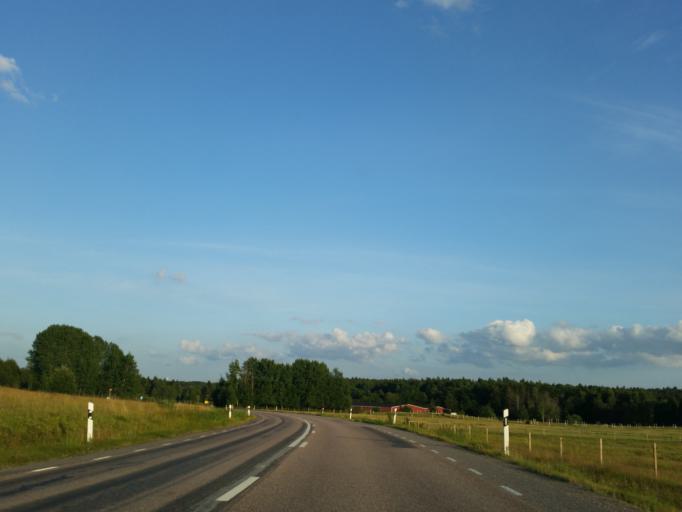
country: SE
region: Stockholm
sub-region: Sodertalje Kommun
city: Soedertaelje
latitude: 59.2228
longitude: 17.5653
